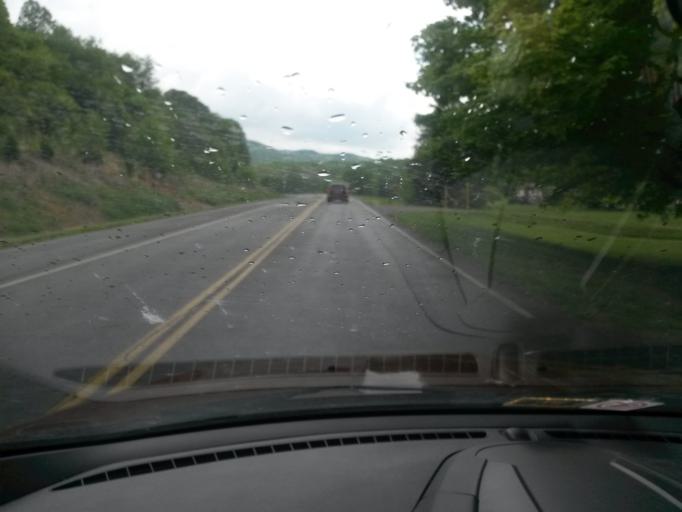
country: US
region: Virginia
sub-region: Botetourt County
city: Cloverdale
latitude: 37.3636
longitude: -79.8995
